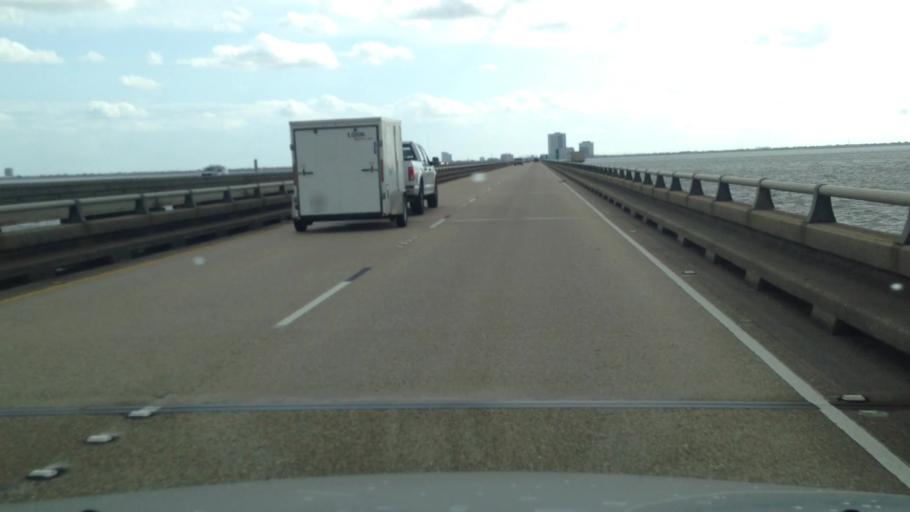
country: US
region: Louisiana
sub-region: Jefferson Parish
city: Metairie
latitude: 30.0574
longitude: -90.1479
